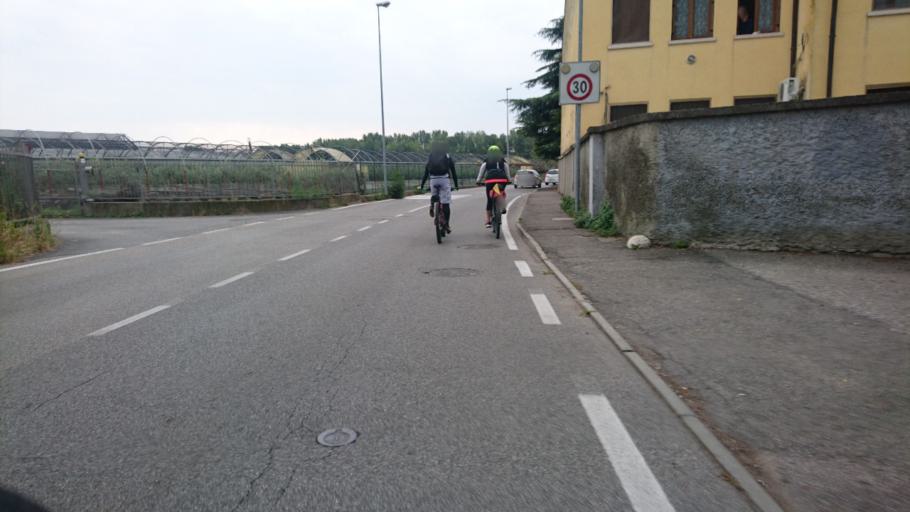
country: IT
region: Veneto
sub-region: Provincia di Verona
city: Verona
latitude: 45.4306
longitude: 11.0213
